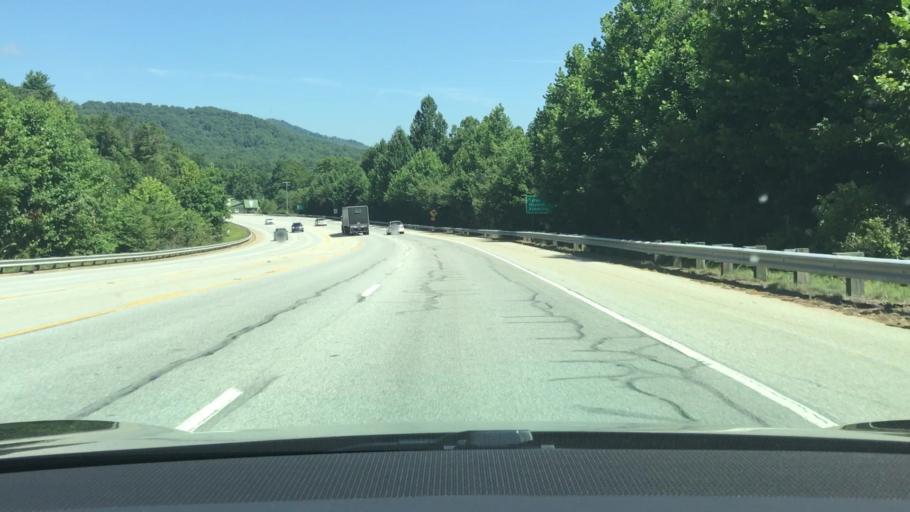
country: US
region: Georgia
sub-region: Rabun County
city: Mountain City
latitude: 35.0066
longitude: -83.3838
